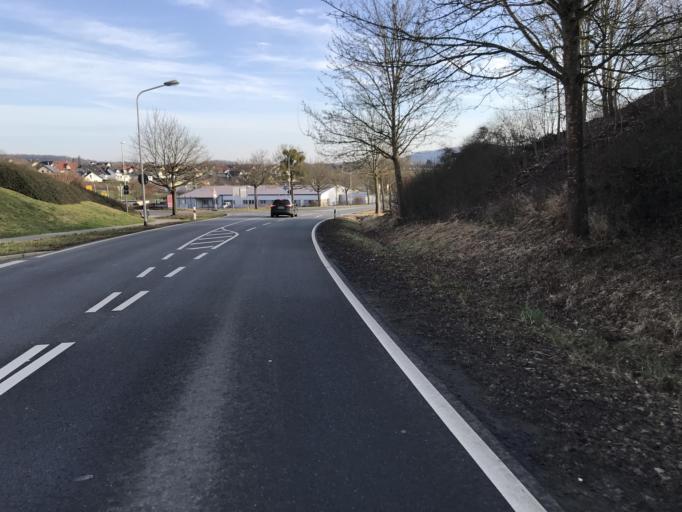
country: DE
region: Hesse
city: Weilburg
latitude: 50.4785
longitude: 8.2892
